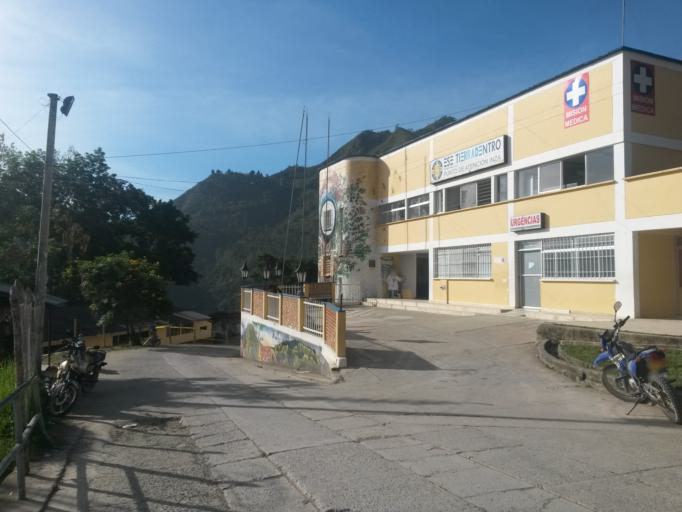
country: CO
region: Cauca
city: Inza
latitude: 2.5489
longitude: -76.0622
